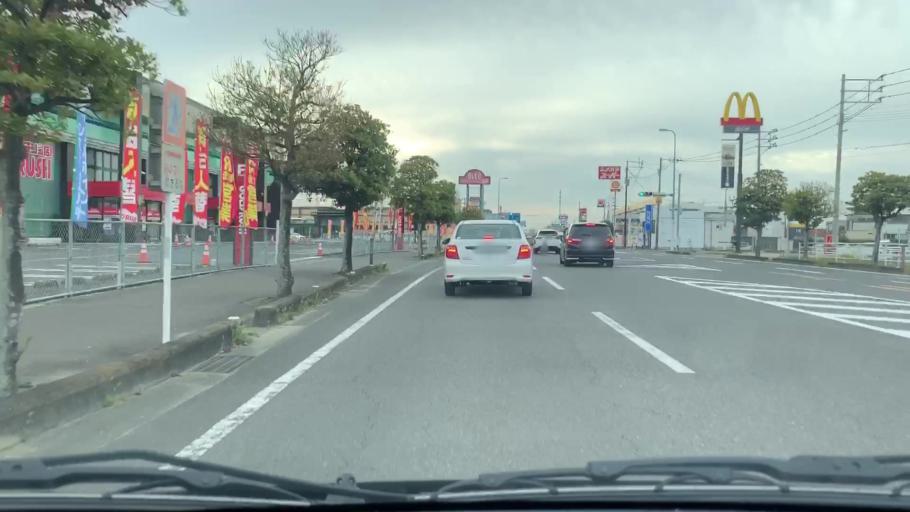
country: JP
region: Saga Prefecture
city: Saga-shi
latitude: 33.2937
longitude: 130.2846
